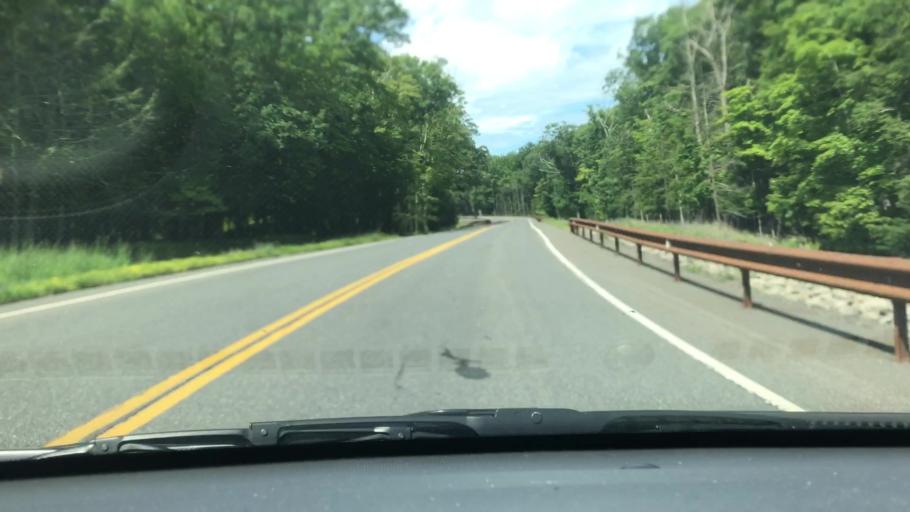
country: US
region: New York
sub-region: Ulster County
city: Shokan
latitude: 41.9356
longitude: -74.2131
